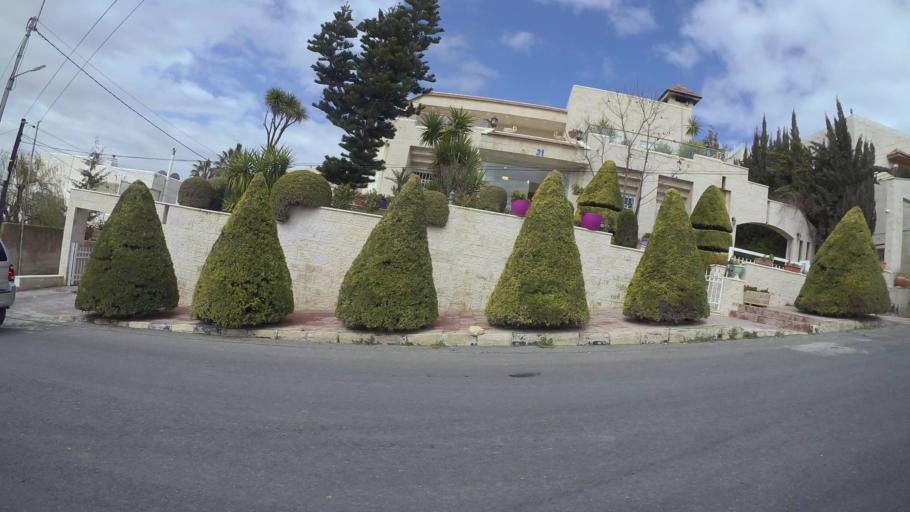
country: JO
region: Amman
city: Al Jubayhah
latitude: 32.0016
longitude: 35.8430
